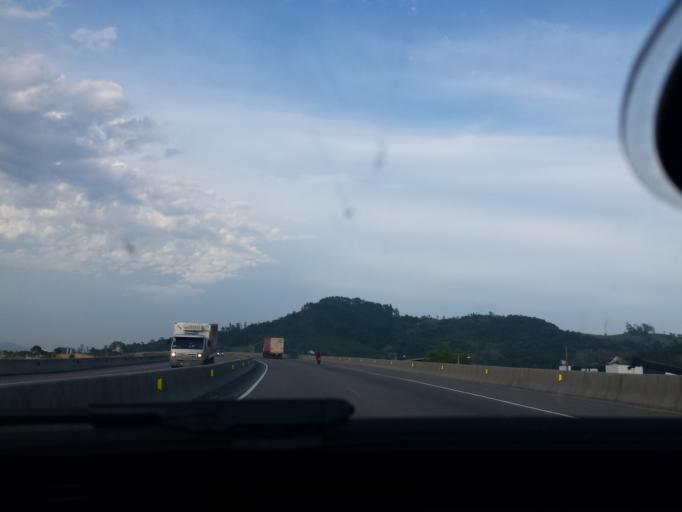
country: BR
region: Santa Catarina
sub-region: Tubarao
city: Tubarao
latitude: -28.4244
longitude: -48.9402
